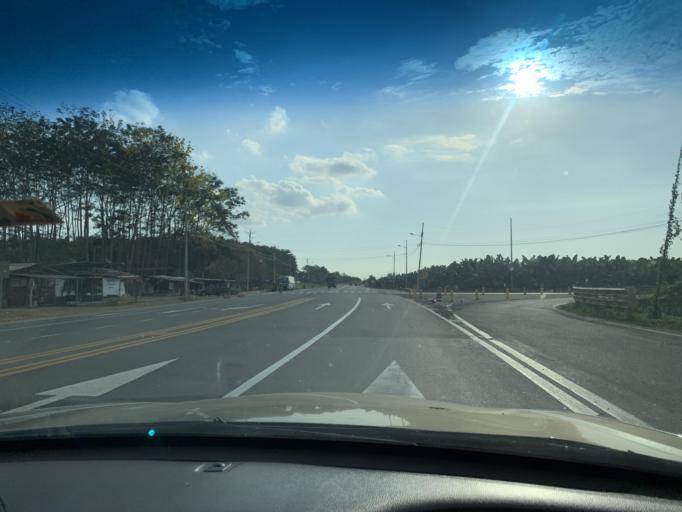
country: EC
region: Guayas
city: Naranjito
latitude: -2.2569
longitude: -79.5608
